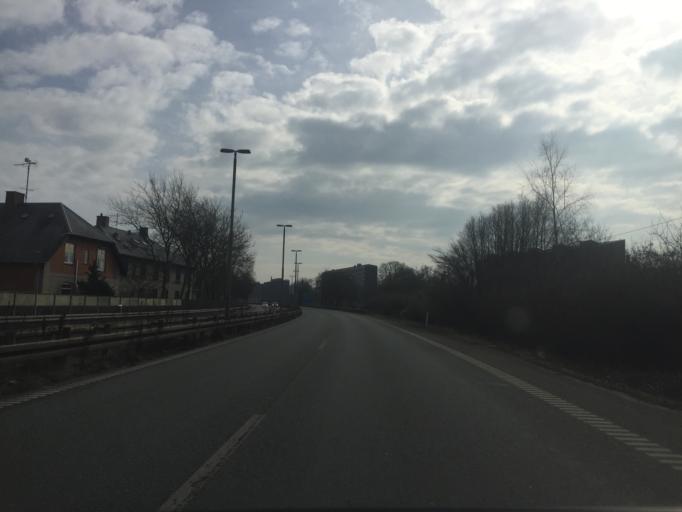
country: DK
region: Capital Region
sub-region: Lyngby-Tarbaek Kommune
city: Kongens Lyngby
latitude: 55.7718
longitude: 12.4959
